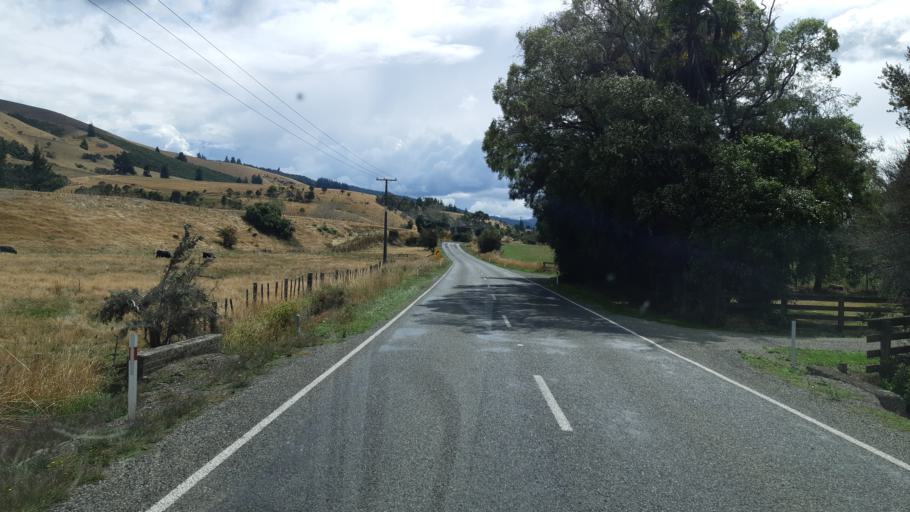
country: NZ
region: Tasman
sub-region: Tasman District
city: Wakefield
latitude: -41.5099
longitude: 172.7952
